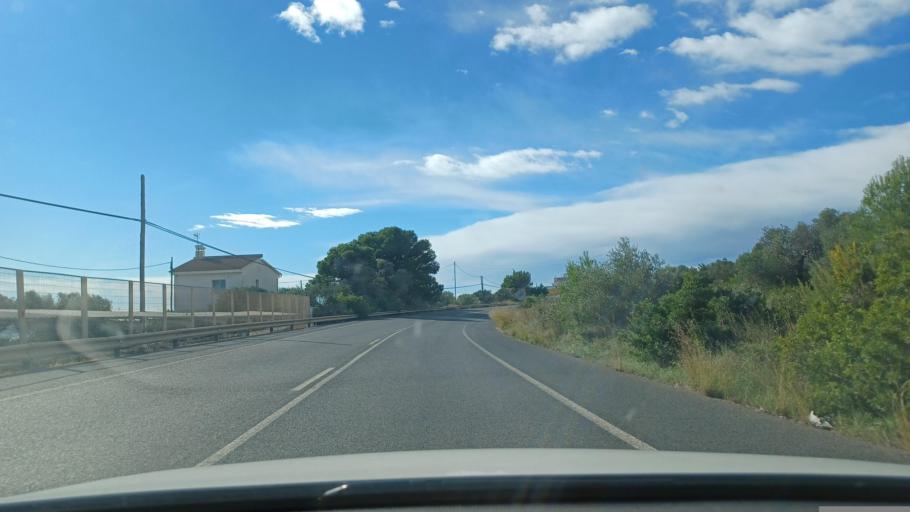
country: ES
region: Catalonia
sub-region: Provincia de Tarragona
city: Sant Carles de la Rapita
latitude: 40.5817
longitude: 0.5552
